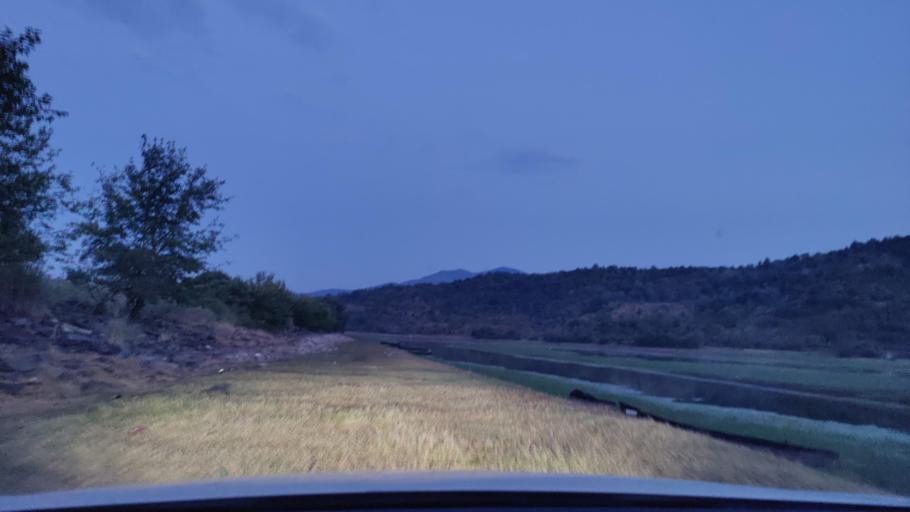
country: GR
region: Central Macedonia
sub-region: Nomos Serron
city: Chrysochorafa
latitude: 41.2032
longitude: 23.0792
